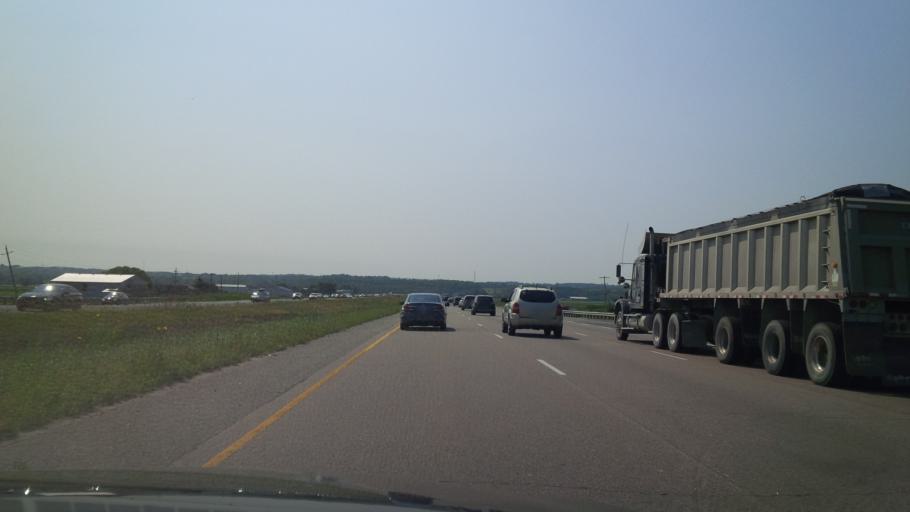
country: CA
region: Ontario
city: Bradford West Gwillimbury
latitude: 44.0493
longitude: -79.6069
